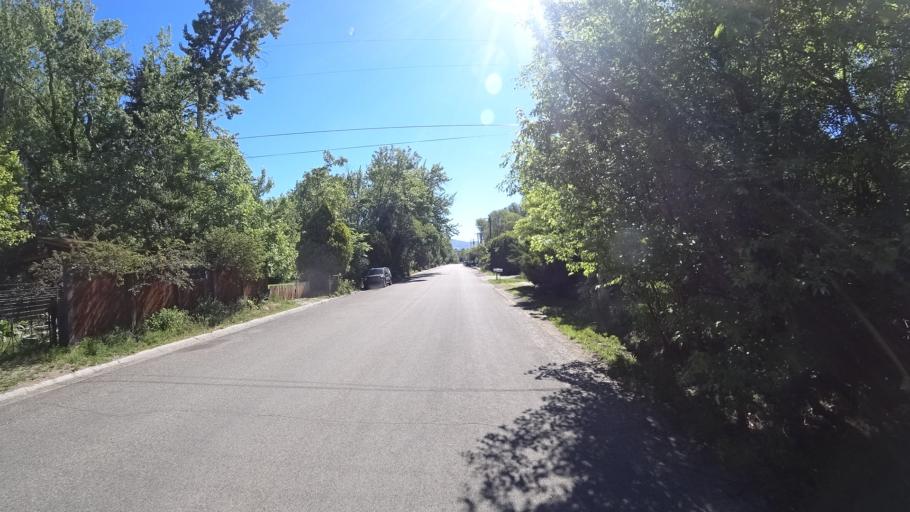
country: US
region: Idaho
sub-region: Ada County
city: Garden City
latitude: 43.6483
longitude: -116.2394
